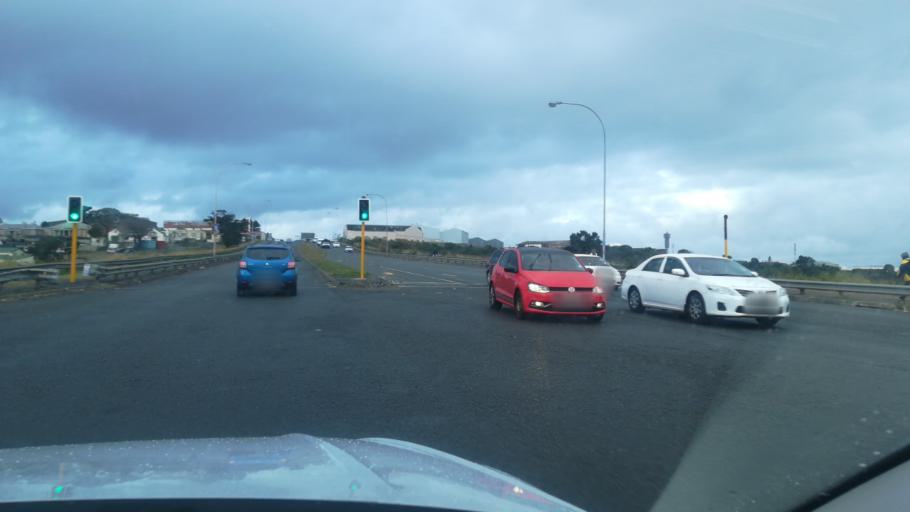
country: ZA
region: Eastern Cape
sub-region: Buffalo City Metropolitan Municipality
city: East London
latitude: -33.0067
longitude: 27.8857
